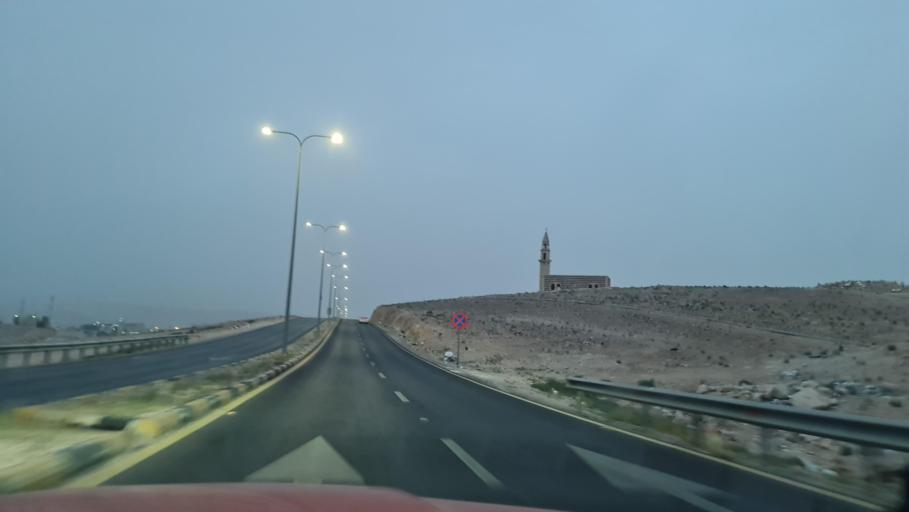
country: JO
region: Zarqa
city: Zarqa
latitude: 32.0468
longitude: 36.1065
